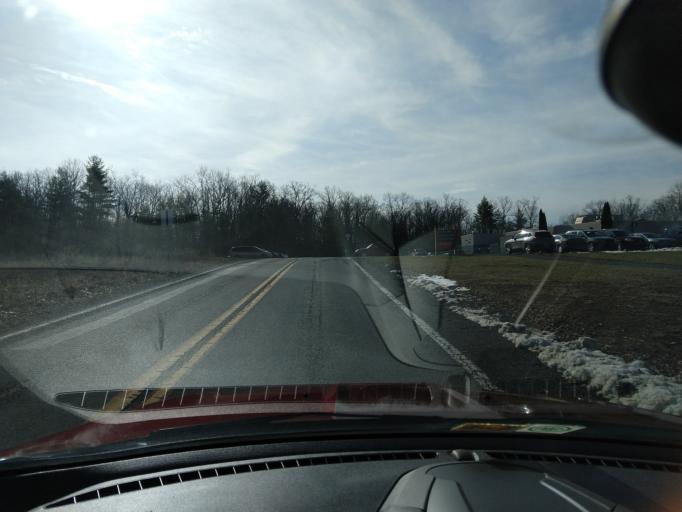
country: US
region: West Virginia
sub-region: Pocahontas County
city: Marlinton
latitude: 38.2018
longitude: -80.1091
